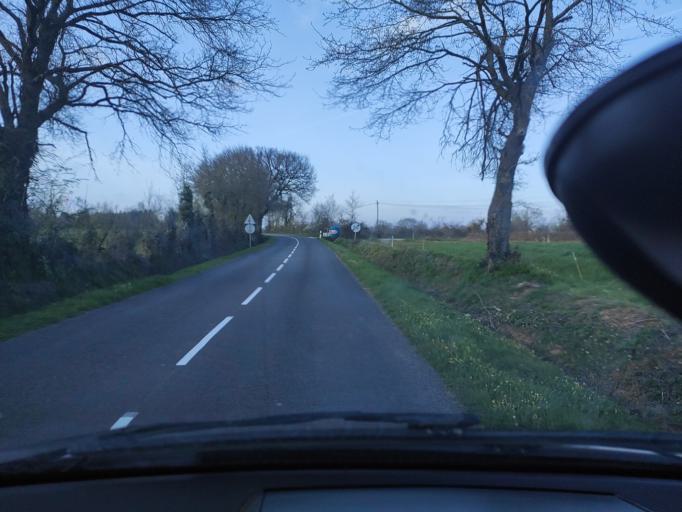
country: FR
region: Pays de la Loire
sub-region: Departement de la Vendee
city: La Chaize-le-Vicomte
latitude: 46.6334
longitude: -1.3032
